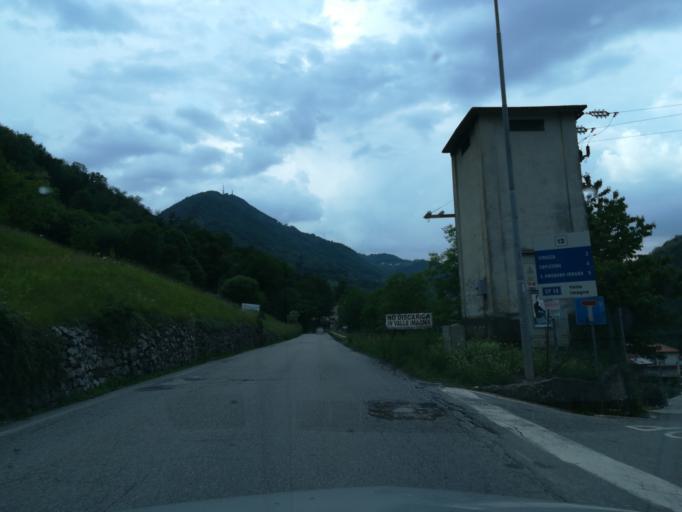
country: IT
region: Lombardy
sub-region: Provincia di Bergamo
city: Almenno San Salvatore
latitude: 45.7612
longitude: 9.5931
